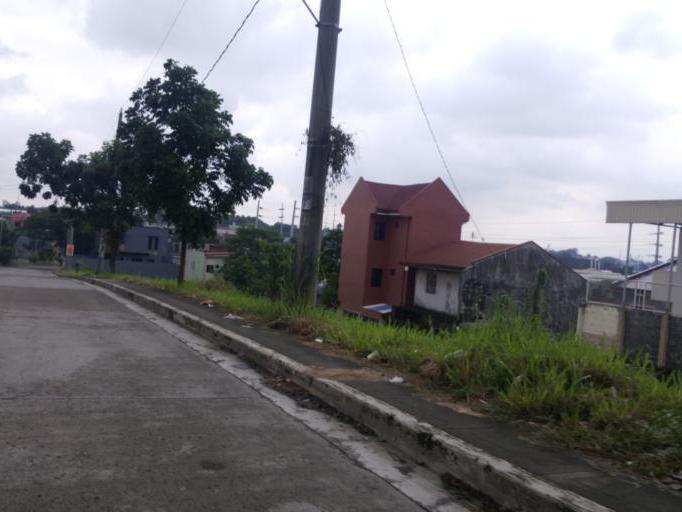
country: PH
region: Calabarzon
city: Bagong Pagasa
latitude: 14.7145
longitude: 121.0208
